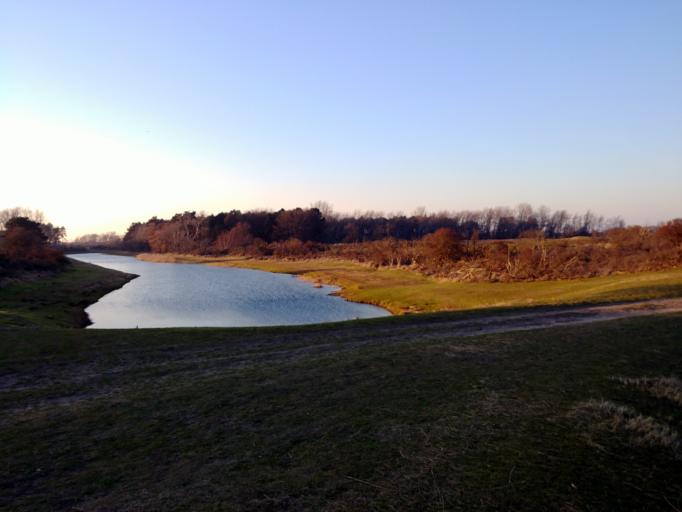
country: NL
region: North Holland
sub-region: Gemeente Zandvoort
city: Zandvoort
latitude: 52.3421
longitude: 4.5403
